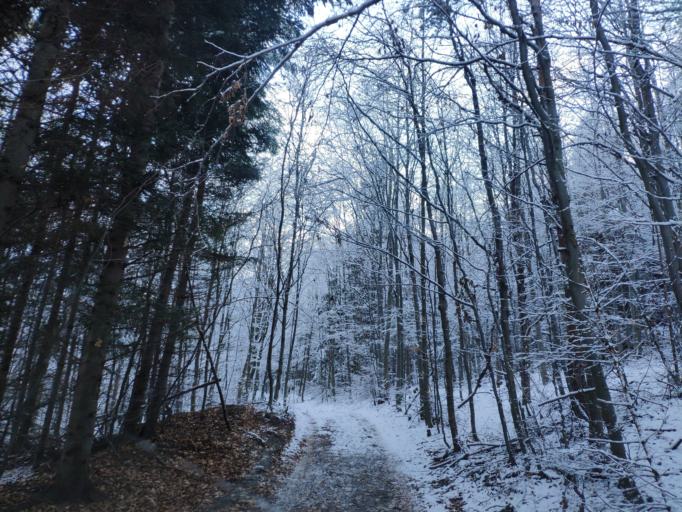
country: SK
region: Kosicky
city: Moldava nad Bodvou
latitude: 48.7452
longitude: 21.0895
